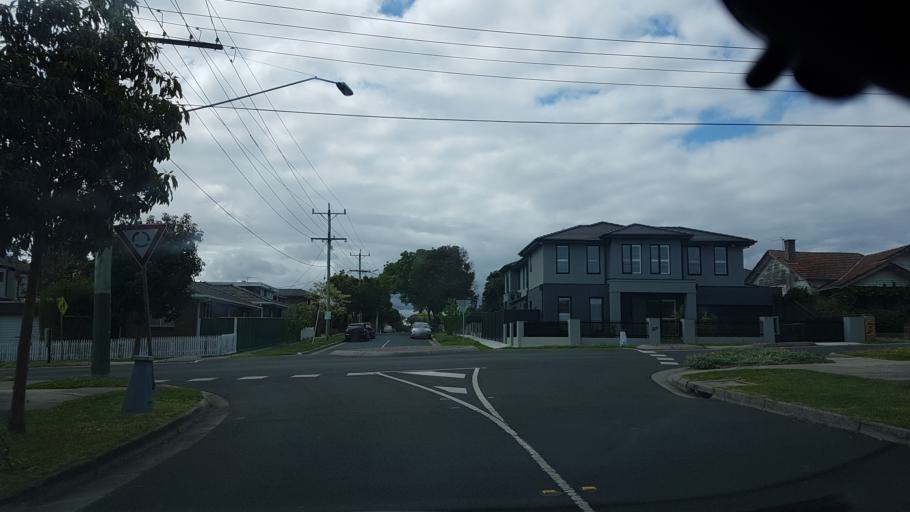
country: AU
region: Victoria
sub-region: Glen Eira
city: Bentleigh
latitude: -37.9228
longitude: 145.0398
